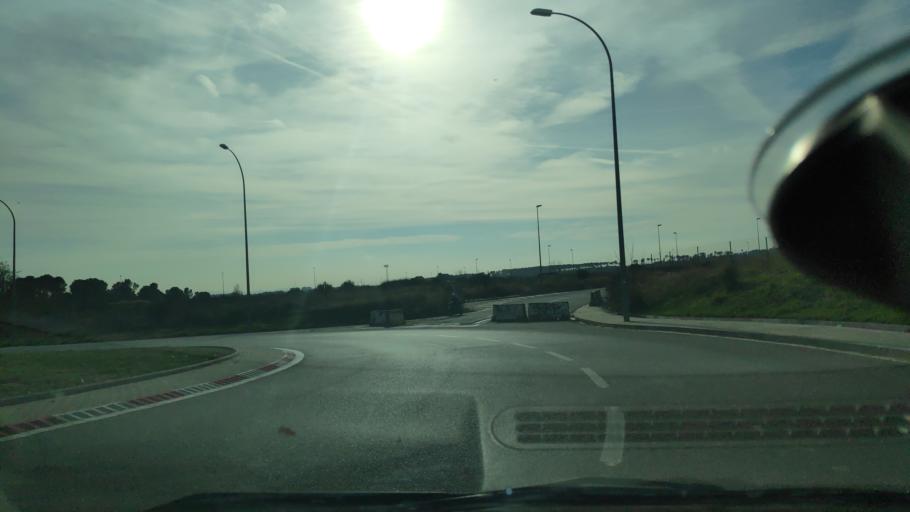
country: ES
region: Catalonia
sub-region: Provincia de Barcelona
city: Castellar del Valles
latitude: 41.5948
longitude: 2.0877
